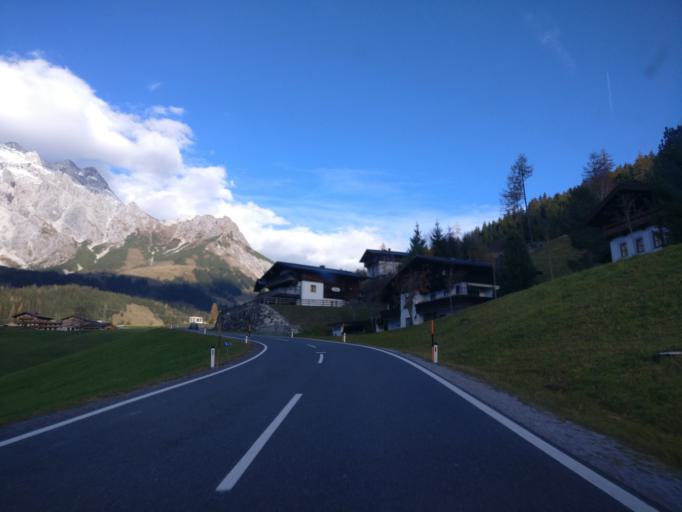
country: AT
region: Salzburg
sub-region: Politischer Bezirk Zell am See
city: Dienten am Hochkonig
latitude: 47.3862
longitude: 13.0213
